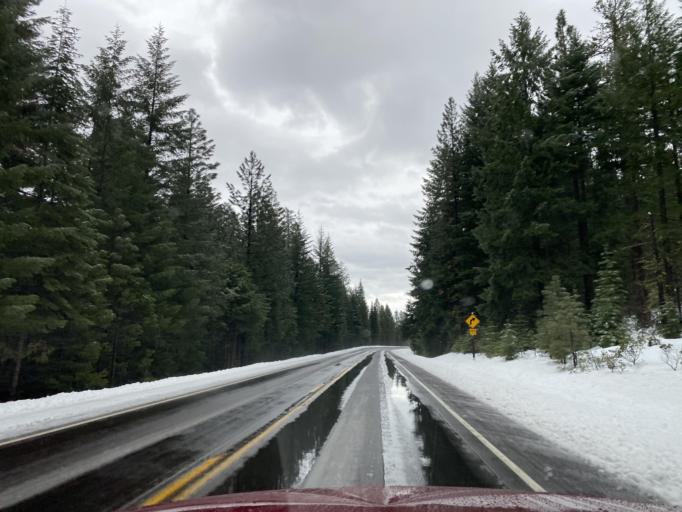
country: US
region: Oregon
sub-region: Klamath County
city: Klamath Falls
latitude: 42.5237
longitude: -122.0864
